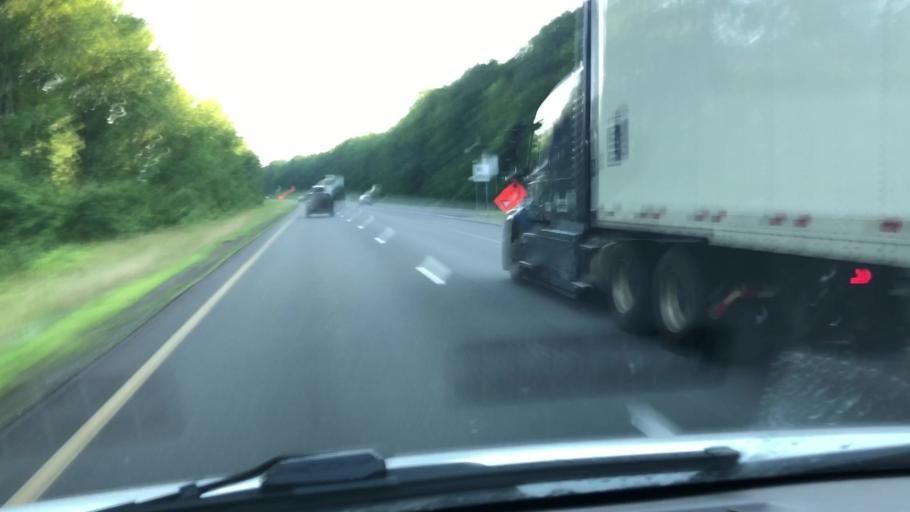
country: US
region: Massachusetts
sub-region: Franklin County
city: South Deerfield
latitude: 42.4863
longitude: -72.6159
